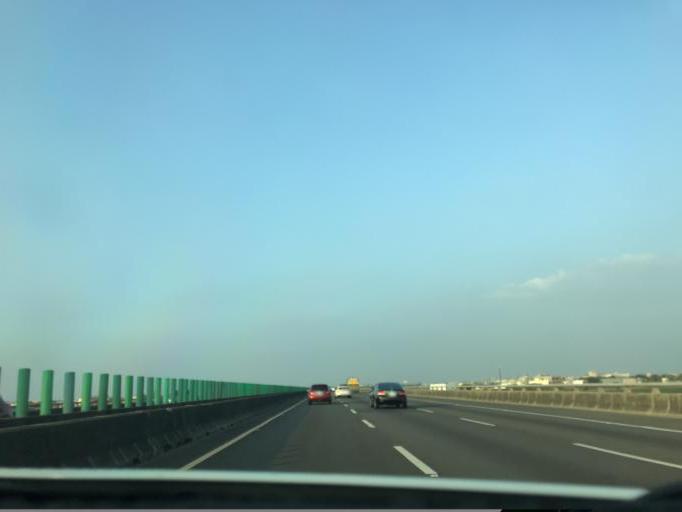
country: TW
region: Taiwan
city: Xinying
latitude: 23.2614
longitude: 120.2599
